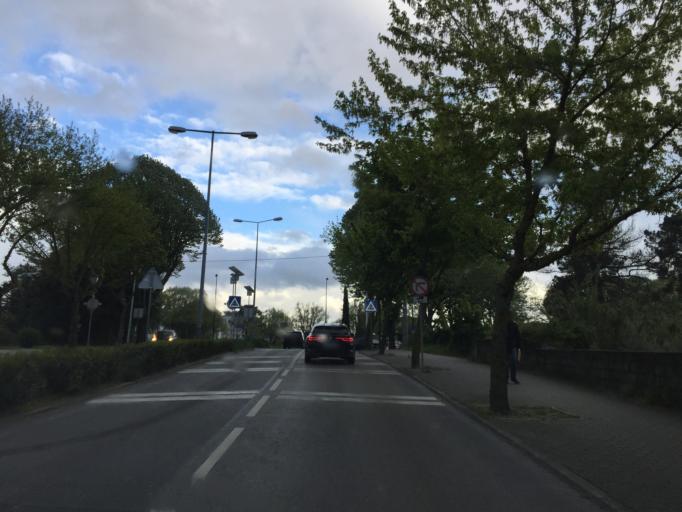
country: PT
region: Viseu
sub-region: Viseu
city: Viseu
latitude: 40.6503
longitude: -7.9204
